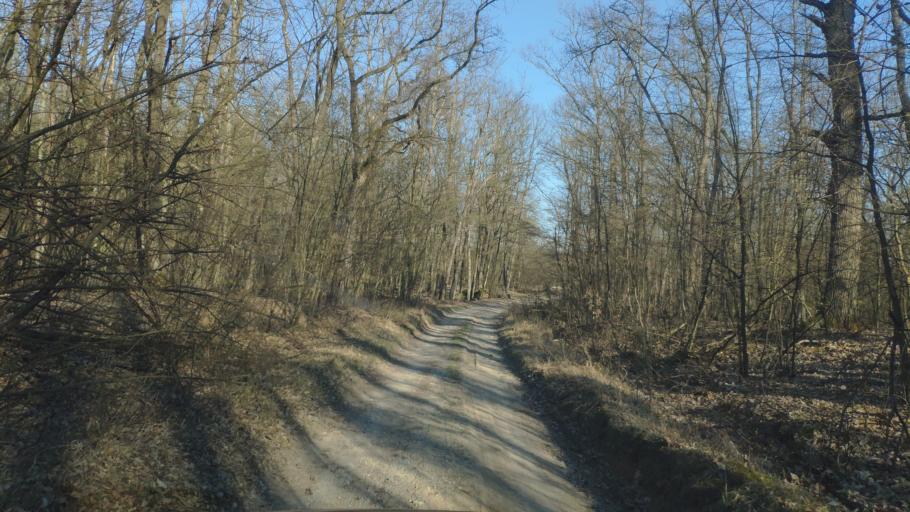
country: HU
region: Borsod-Abauj-Zemplen
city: Putnok
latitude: 48.5015
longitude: 20.2977
